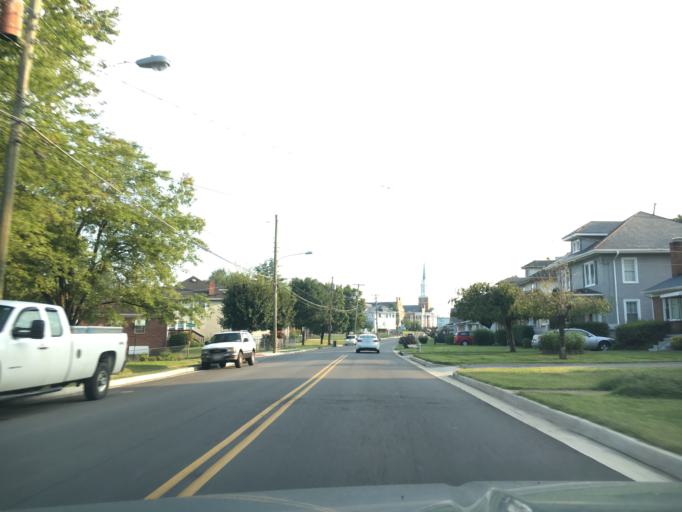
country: US
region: Virginia
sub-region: City of Lynchburg
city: West Lynchburg
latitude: 37.3941
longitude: -79.1719
